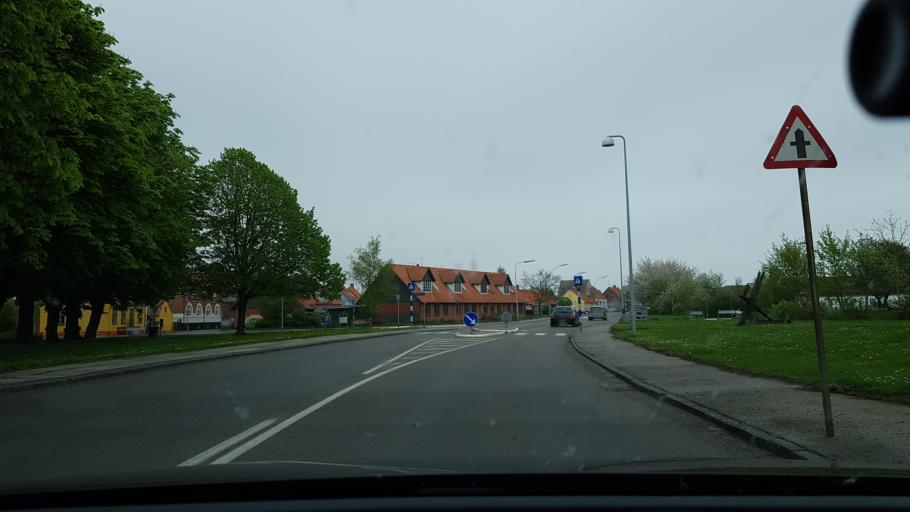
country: DK
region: Capital Region
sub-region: Bornholm Kommune
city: Nexo
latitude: 55.0569
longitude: 15.1274
